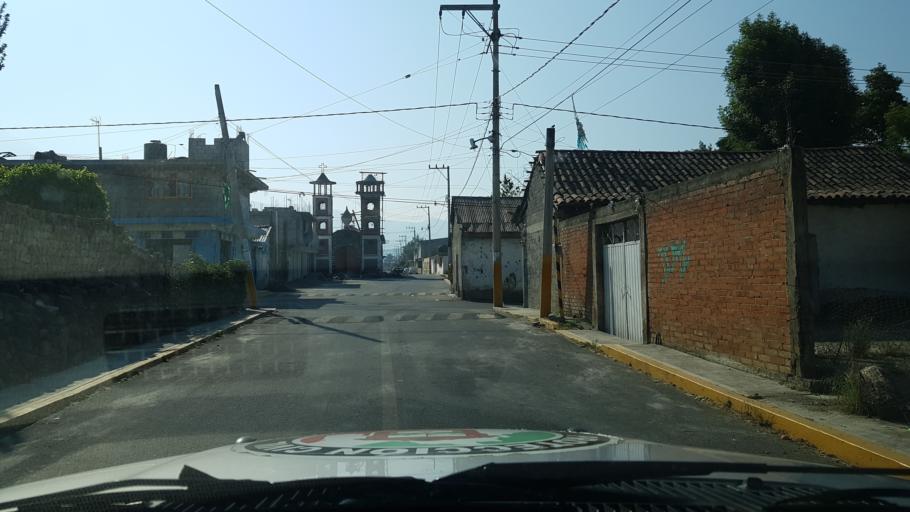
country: MX
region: Mexico
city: Atlautla
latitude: 19.0325
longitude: -98.7803
